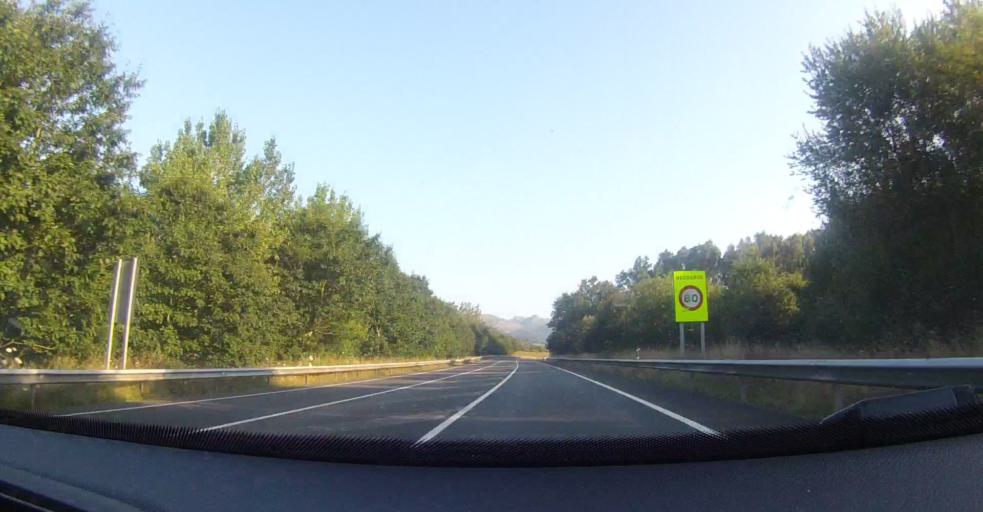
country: ES
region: Cantabria
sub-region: Provincia de Cantabria
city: Ampuero
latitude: 43.3250
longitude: -3.4091
